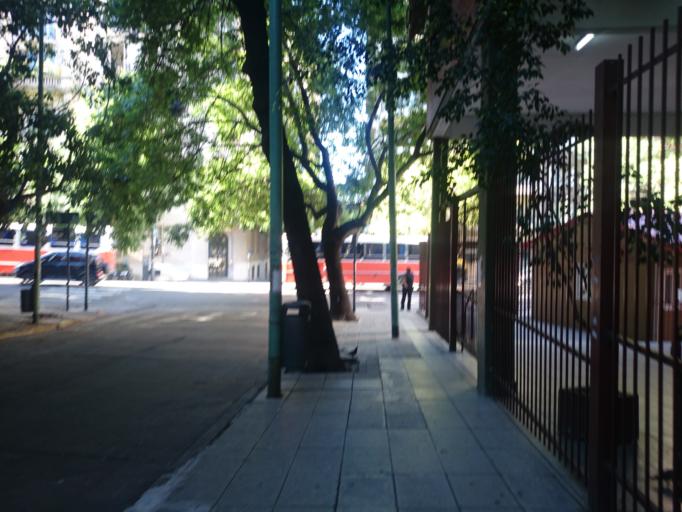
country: AR
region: Buenos Aires F.D.
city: Retiro
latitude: -34.5932
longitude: -58.3775
